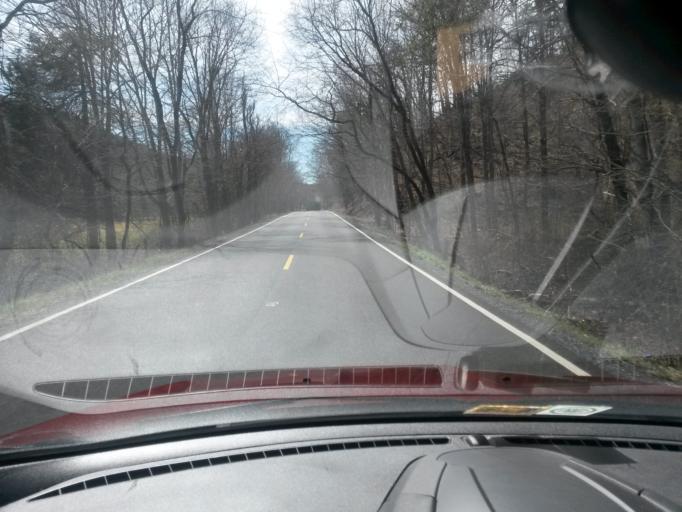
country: US
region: West Virginia
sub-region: Greenbrier County
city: White Sulphur Springs
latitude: 37.7088
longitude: -80.2098
